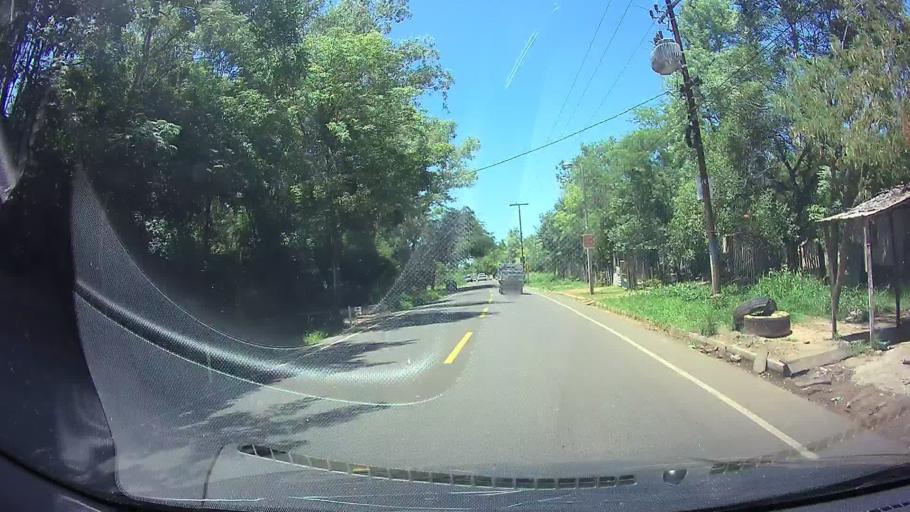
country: PY
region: Central
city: Limpio
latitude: -25.2442
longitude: -57.4912
